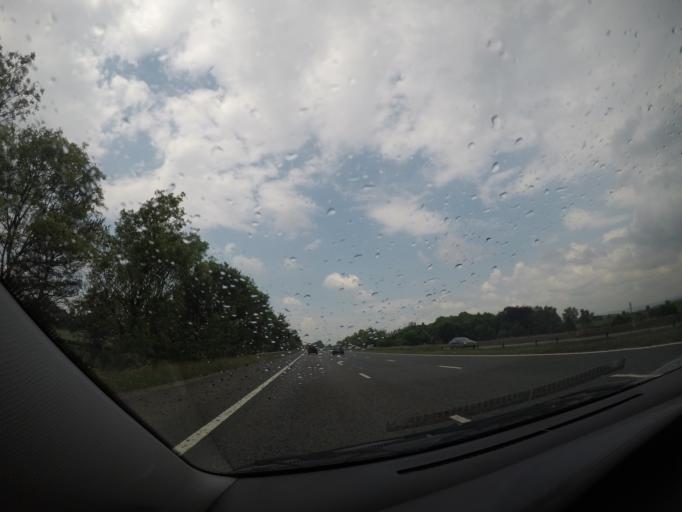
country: GB
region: England
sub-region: Cumbria
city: Penrith
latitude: 54.7415
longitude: -2.8092
